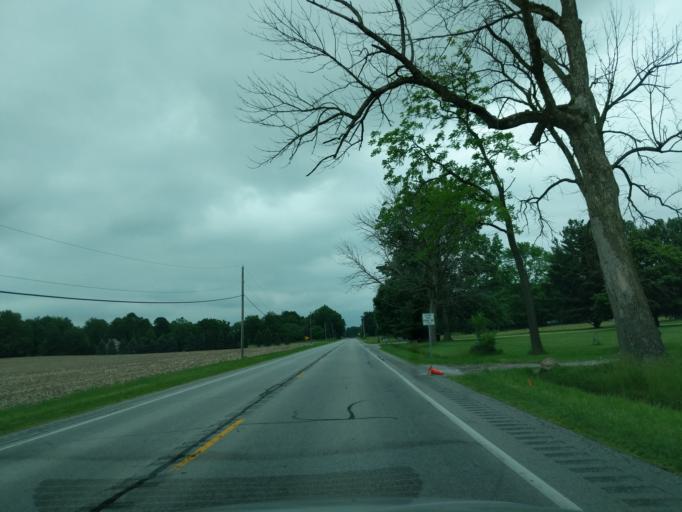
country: US
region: Indiana
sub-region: Madison County
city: Alexandria
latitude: 40.2774
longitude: -85.6988
